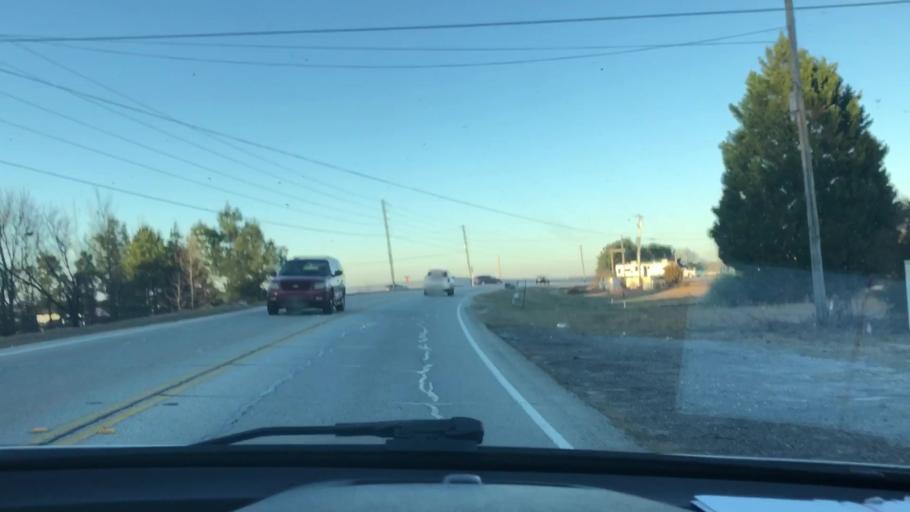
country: US
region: Georgia
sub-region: Walton County
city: Loganville
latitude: 33.8003
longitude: -83.9557
